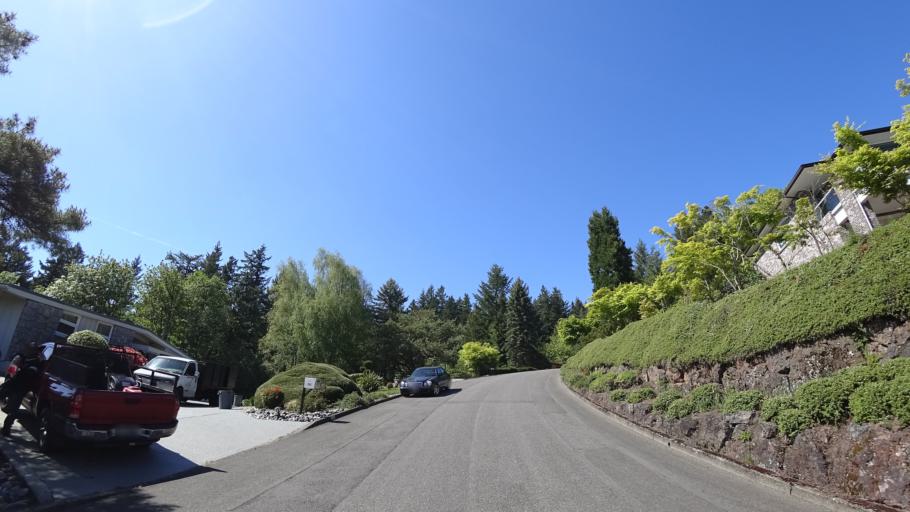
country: US
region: Oregon
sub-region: Washington County
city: West Slope
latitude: 45.5001
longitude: -122.7352
